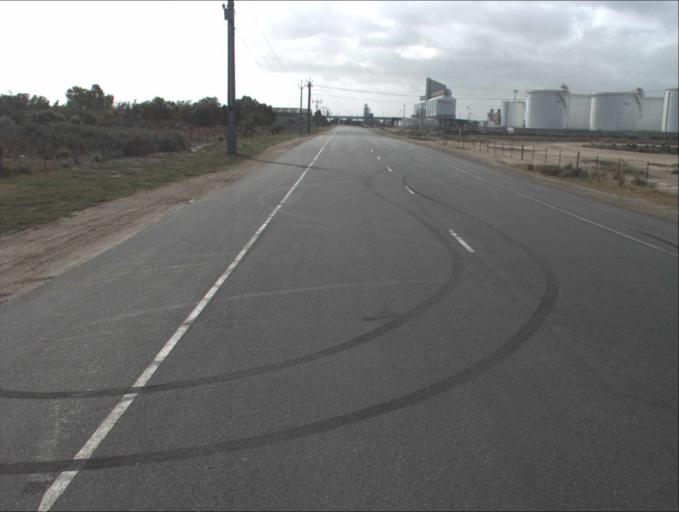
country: AU
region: South Australia
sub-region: Port Adelaide Enfield
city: Birkenhead
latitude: -34.7797
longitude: 138.5015
